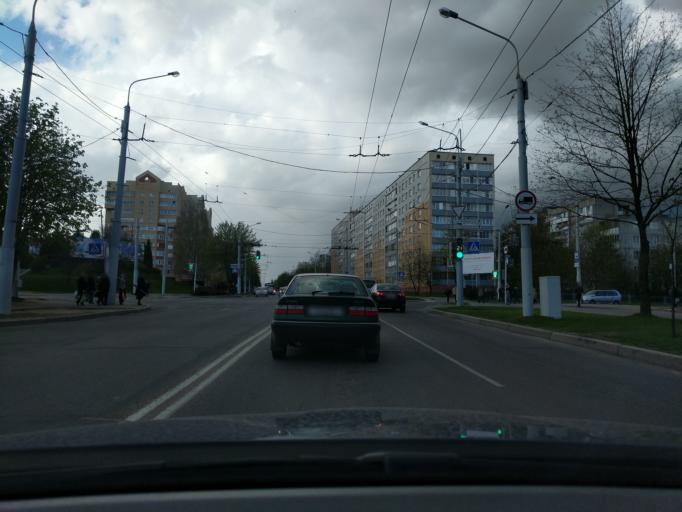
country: BY
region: Minsk
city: Novoye Medvezhino
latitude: 53.9016
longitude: 27.4817
